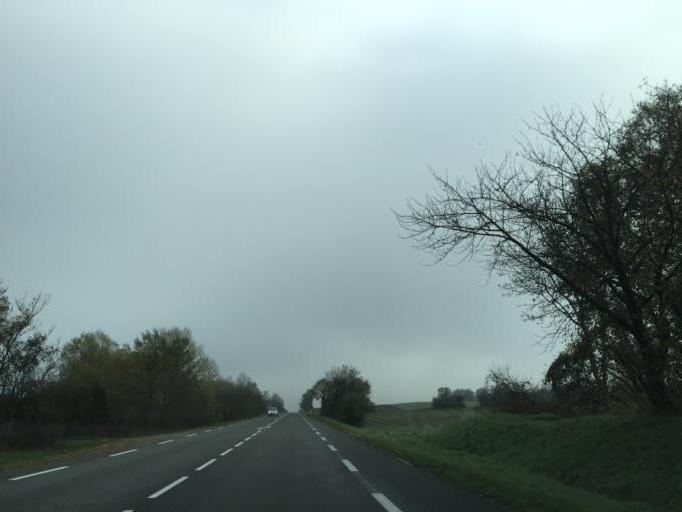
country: FR
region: Rhone-Alpes
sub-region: Departement de l'Ain
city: Saint-Jean-de-Niost
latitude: 45.8577
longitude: 5.2096
